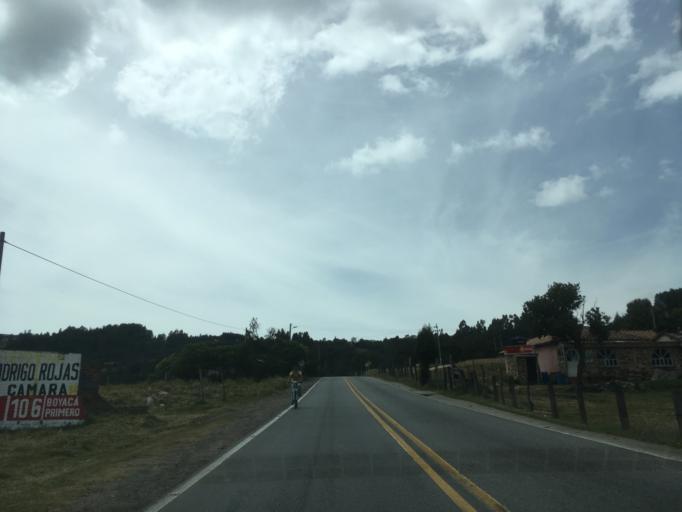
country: CO
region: Boyaca
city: Sogamoso
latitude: 5.6356
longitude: -72.9193
